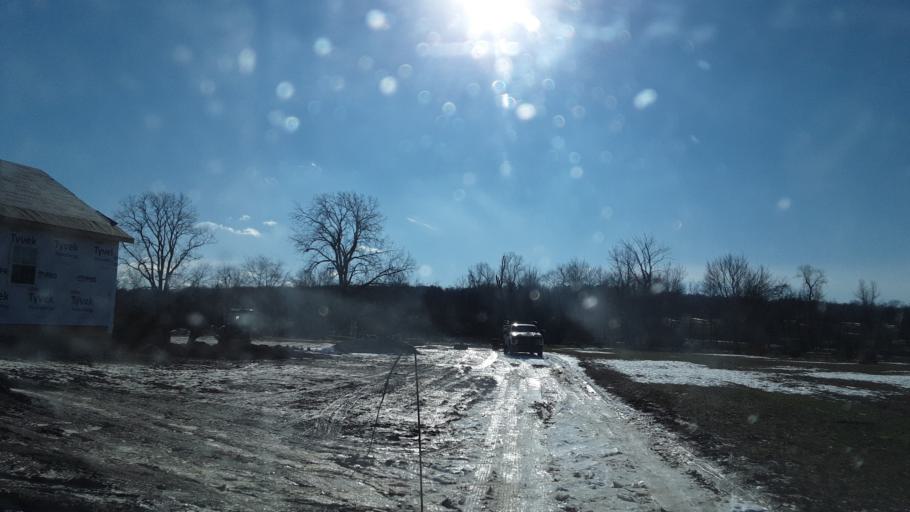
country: US
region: Ohio
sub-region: Richland County
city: Lincoln Heights
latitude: 40.8418
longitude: -82.4858
